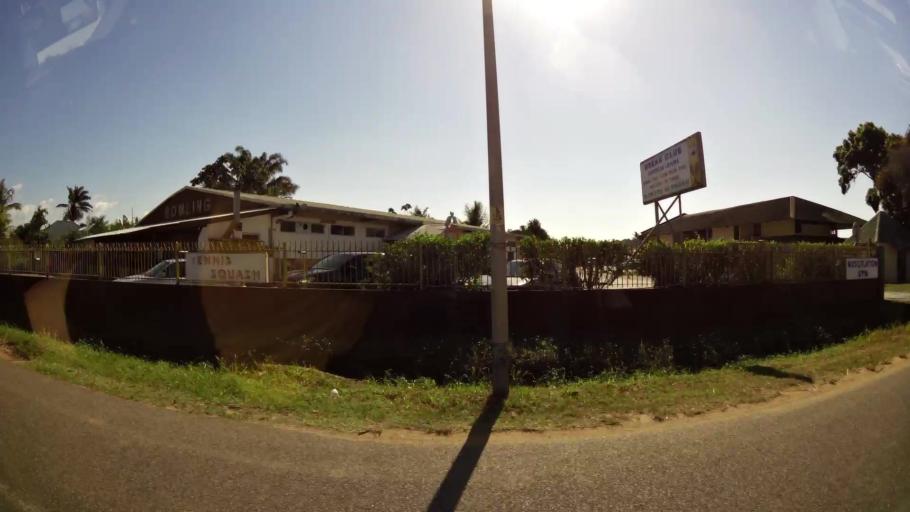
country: GF
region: Guyane
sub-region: Guyane
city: Remire-Montjoly
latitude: 4.8969
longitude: -52.2741
